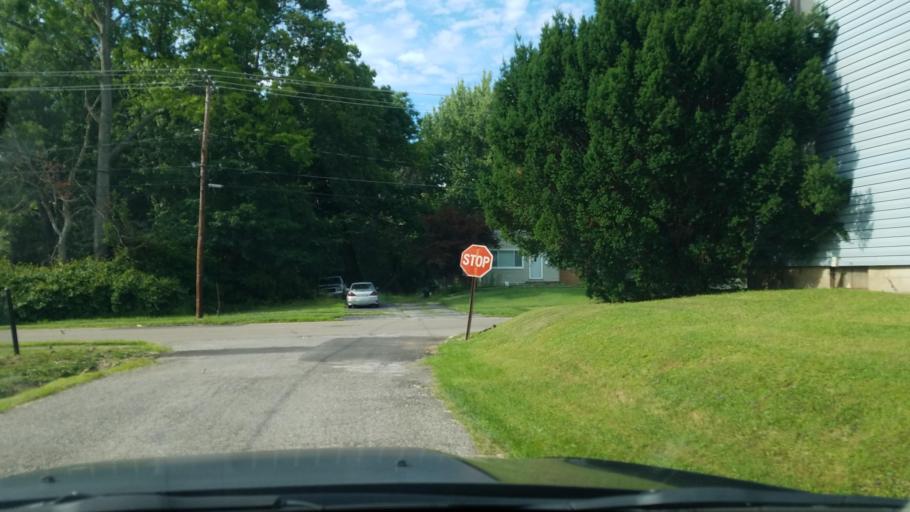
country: US
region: Ohio
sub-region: Trumbull County
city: Niles
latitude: 41.1750
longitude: -80.7763
